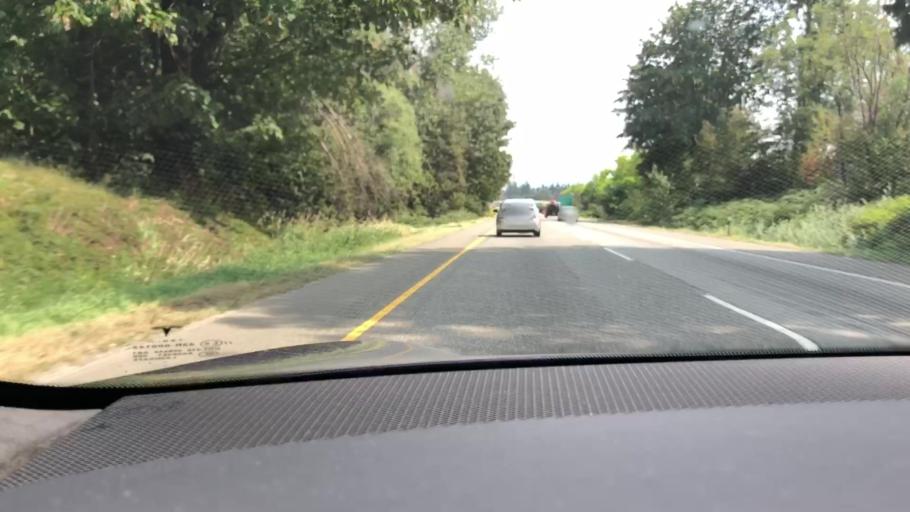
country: US
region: Washington
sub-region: Whatcom County
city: Sumas
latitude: 49.0418
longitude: -122.3459
